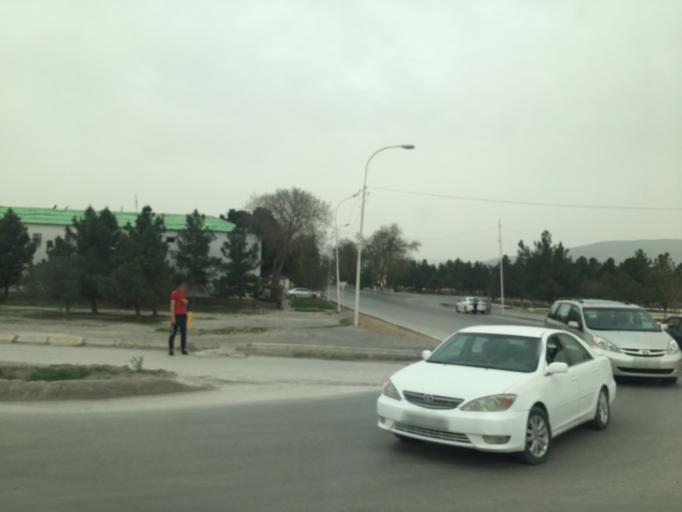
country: TM
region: Ahal
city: Abadan
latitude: 38.1587
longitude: 57.9651
